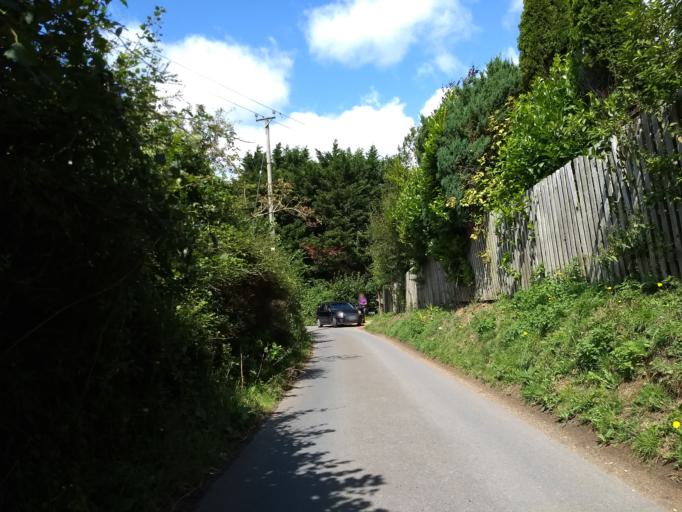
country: GB
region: England
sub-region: Isle of Wight
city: Newport
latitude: 50.6836
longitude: -1.2997
